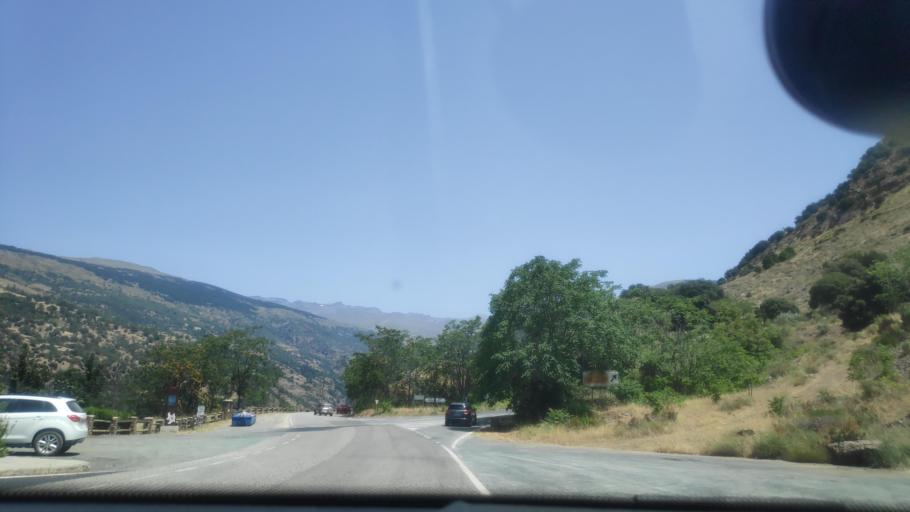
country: ES
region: Andalusia
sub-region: Provincia de Granada
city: Pampaneira
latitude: 36.9296
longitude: -3.3645
